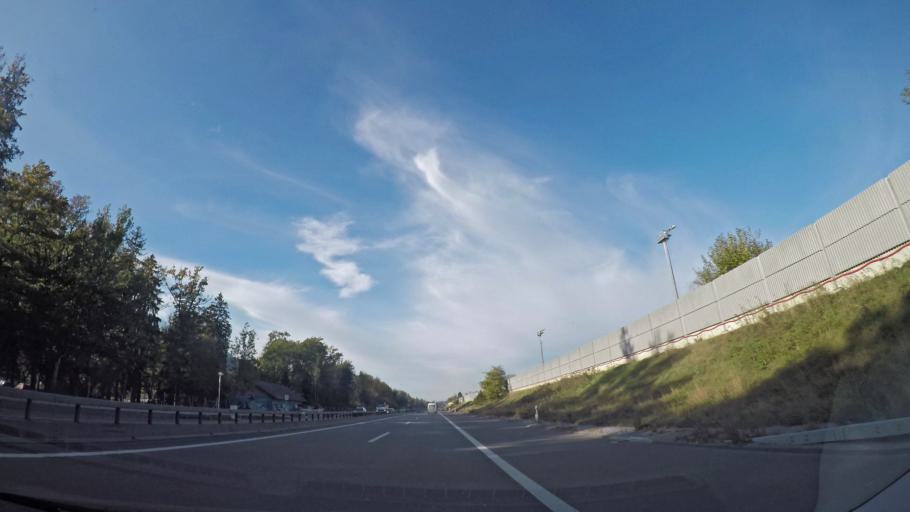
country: CH
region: Bern
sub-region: Bern-Mittelland District
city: Munsingen
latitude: 46.8671
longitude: 7.5489
